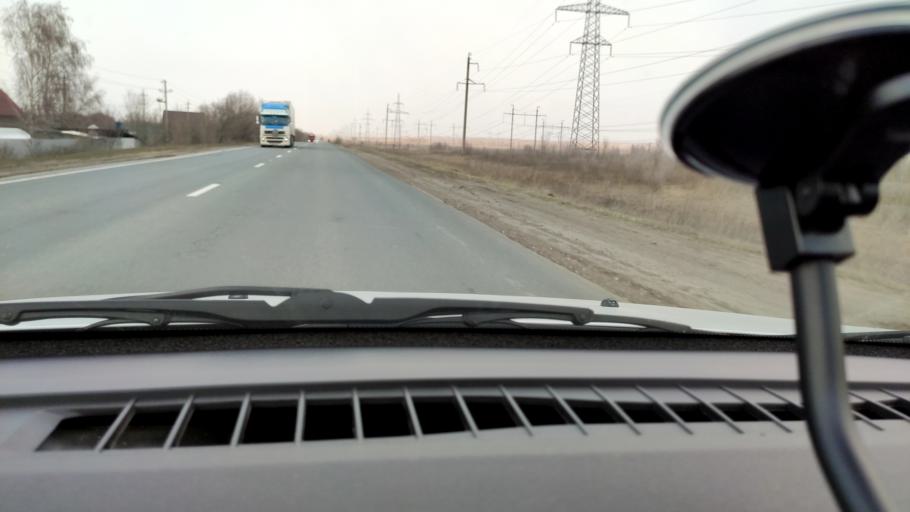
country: RU
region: Samara
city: Dubovyy Umet
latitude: 53.0852
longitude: 50.3929
